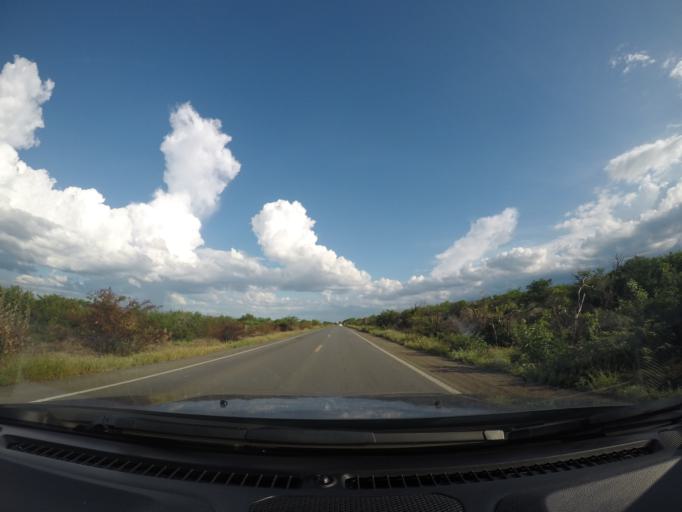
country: BR
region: Bahia
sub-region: Oliveira Dos Brejinhos
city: Oliveira dos Brejinhos
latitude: -12.0801
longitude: -42.9441
